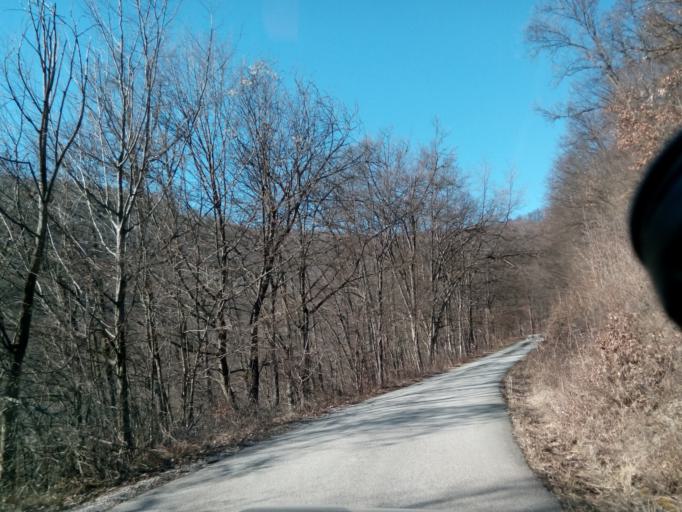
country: SK
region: Kosicky
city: Roznava
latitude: 48.5534
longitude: 20.5680
